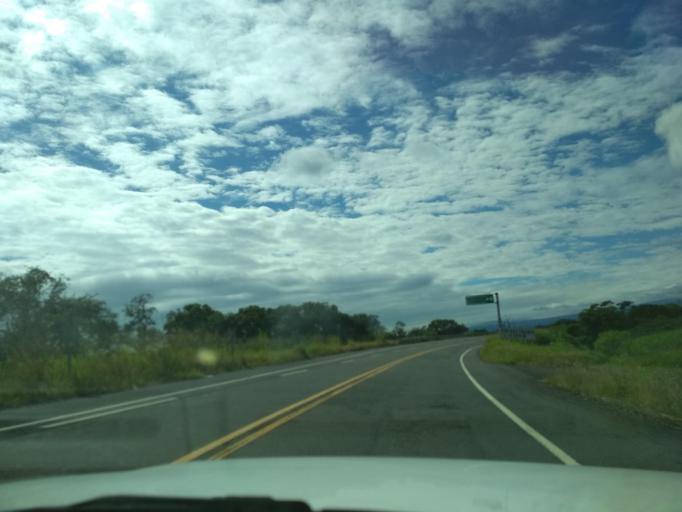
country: MX
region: Veracruz
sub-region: Coatepec
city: Las Lomas
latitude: 19.4488
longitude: -96.9274
